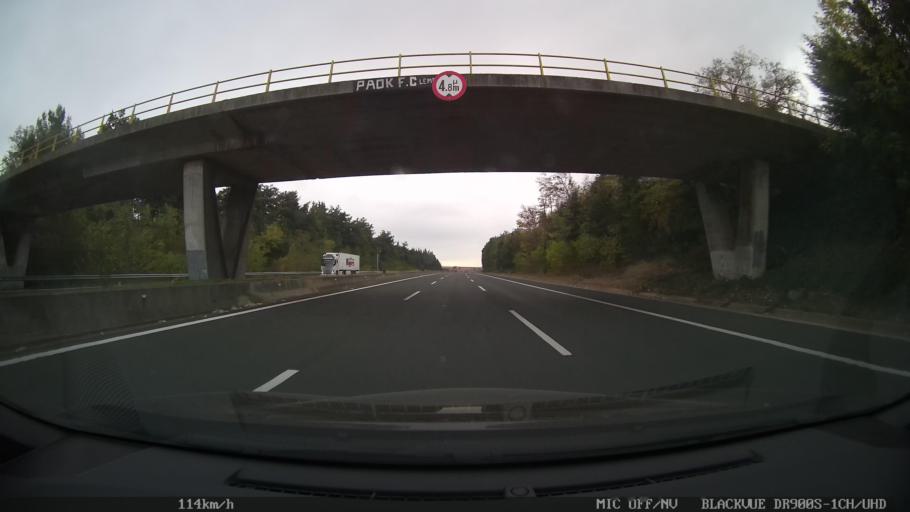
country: GR
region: Central Macedonia
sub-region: Nomos Pierias
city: Kitros
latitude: 40.3805
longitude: 22.6066
